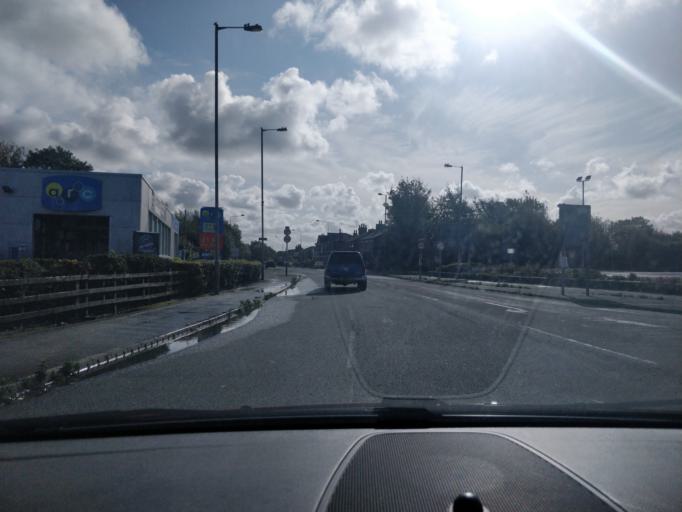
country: GB
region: England
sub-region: Sefton
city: Southport
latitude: 53.6317
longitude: -2.9682
